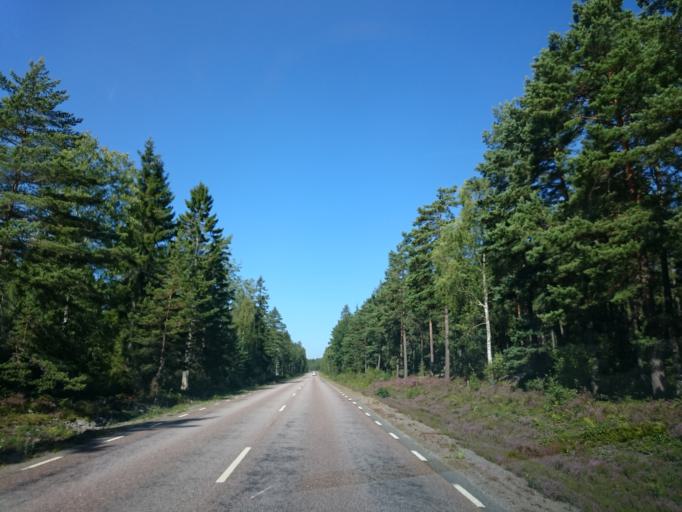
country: SE
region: OEstergoetland
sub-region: Norrkopings Kommun
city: Krokek
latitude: 58.6478
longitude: 16.5684
